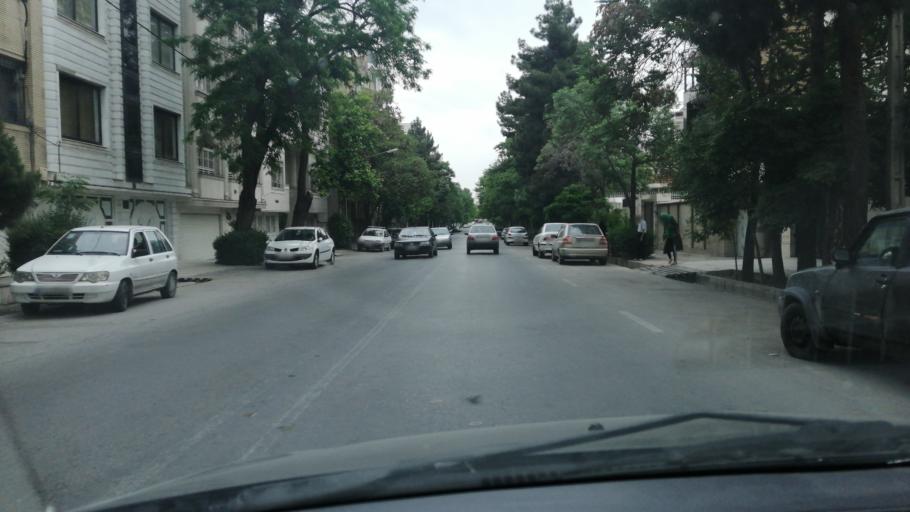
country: IR
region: Razavi Khorasan
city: Mashhad
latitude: 36.2836
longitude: 59.5718
